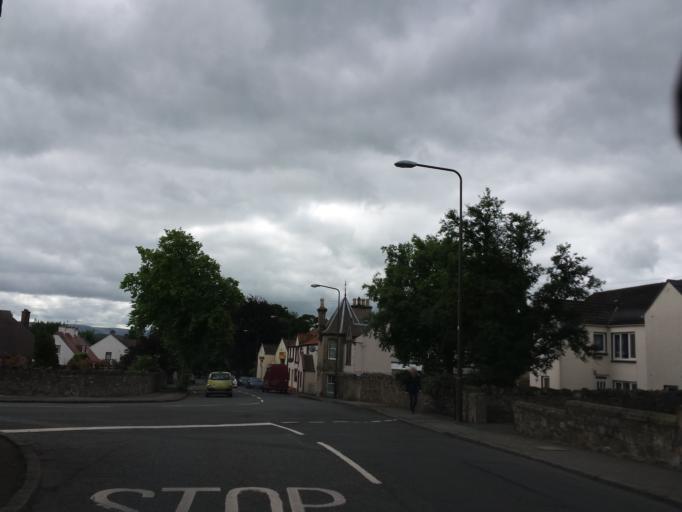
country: GB
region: Scotland
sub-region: East Lothian
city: Haddington
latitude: 55.9604
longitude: -2.7768
